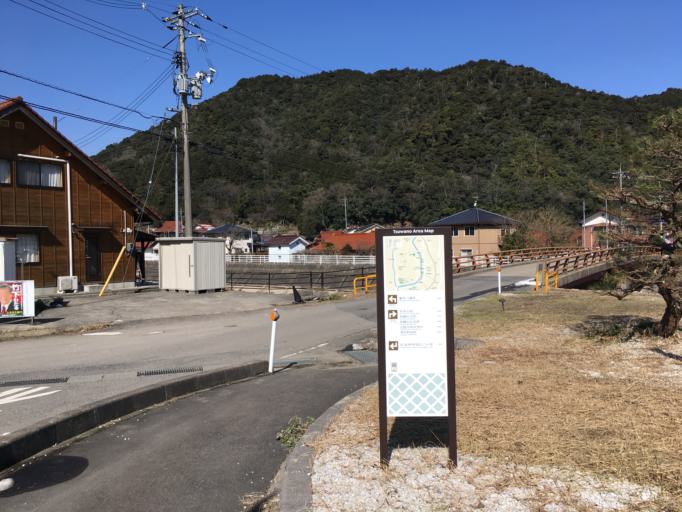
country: JP
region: Shimane
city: Masuda
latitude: 34.4508
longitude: 131.7632
